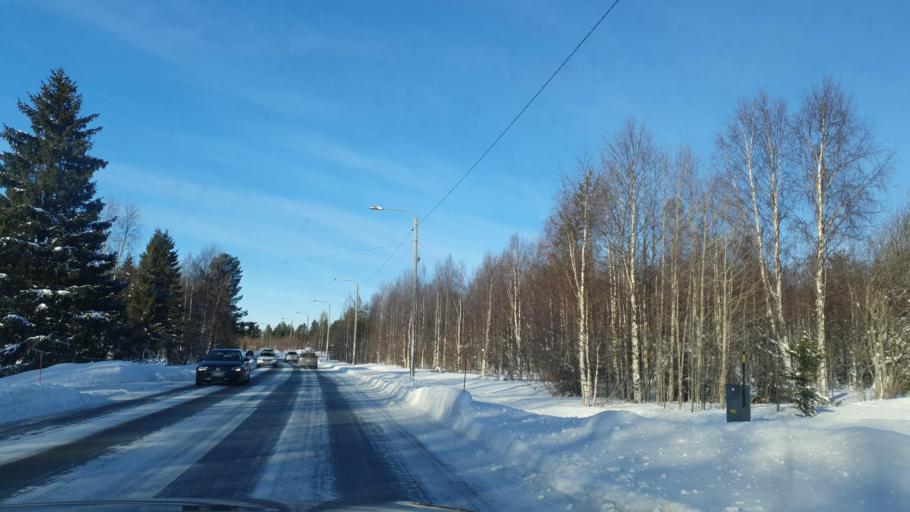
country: FI
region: Lapland
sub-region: Torniolaakso
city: Ylitornio
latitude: 66.2782
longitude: 23.6982
